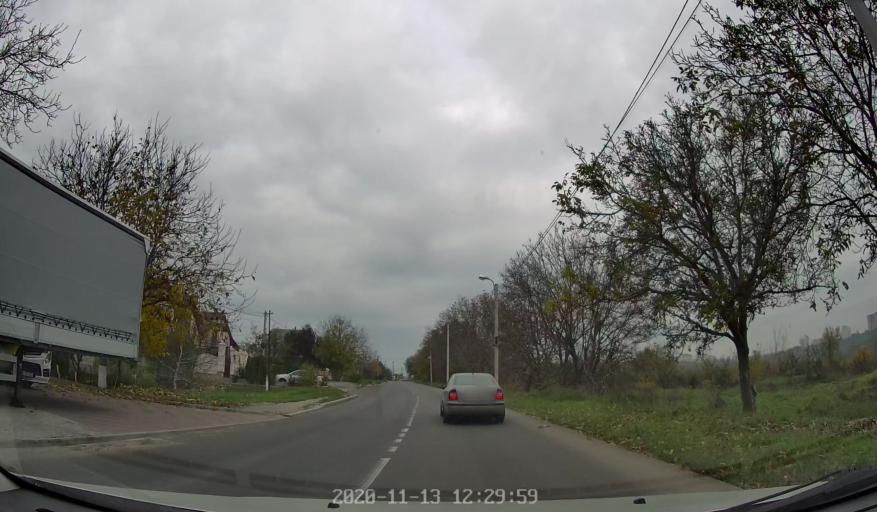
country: MD
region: Chisinau
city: Chisinau
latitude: 46.9662
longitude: 28.8344
